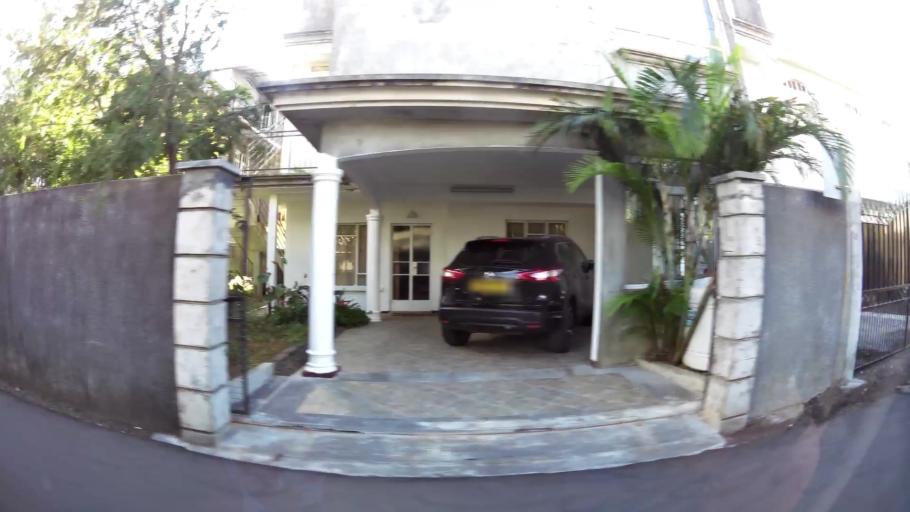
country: MU
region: Plaines Wilhems
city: Curepipe
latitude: -20.2899
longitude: 57.5163
